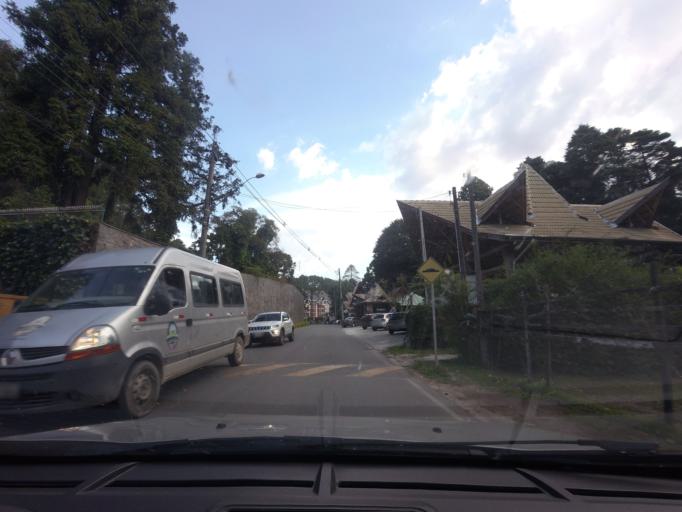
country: BR
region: Sao Paulo
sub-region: Campos Do Jordao
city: Campos do Jordao
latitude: -22.7300
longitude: -45.5698
